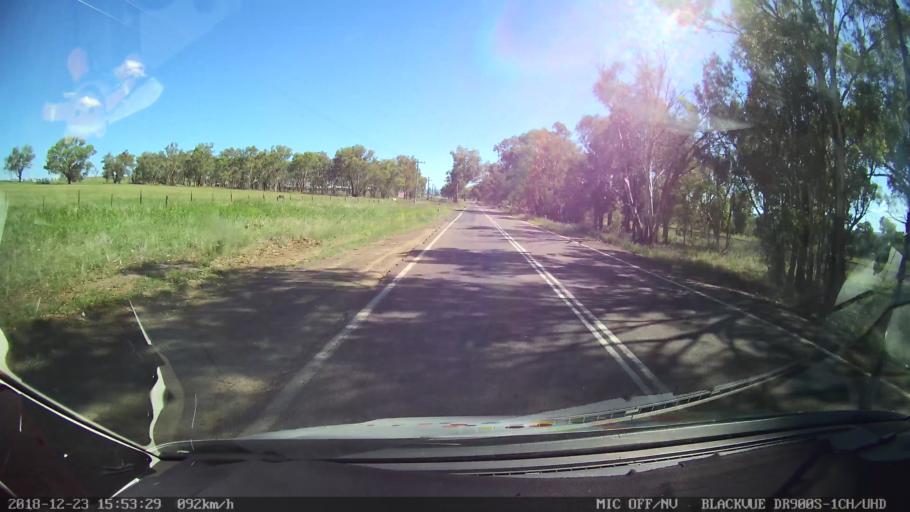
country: AU
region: New South Wales
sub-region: Tamworth Municipality
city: Phillip
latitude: -31.1337
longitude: 150.8806
